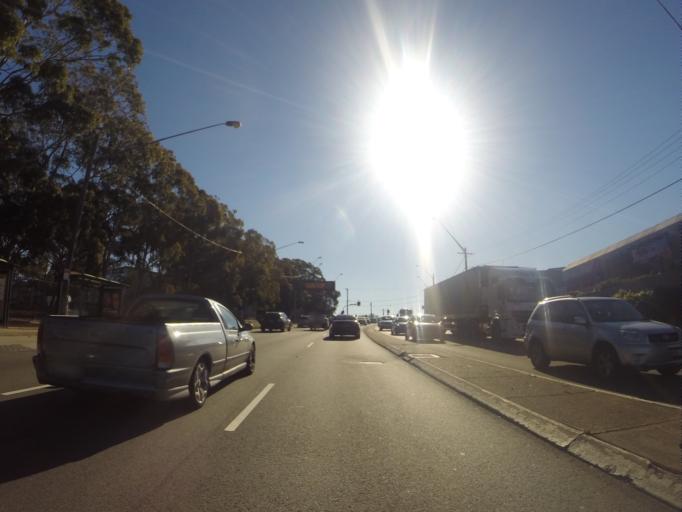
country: AU
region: New South Wales
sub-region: Canterbury
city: Roselands
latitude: -33.9481
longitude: 151.0795
